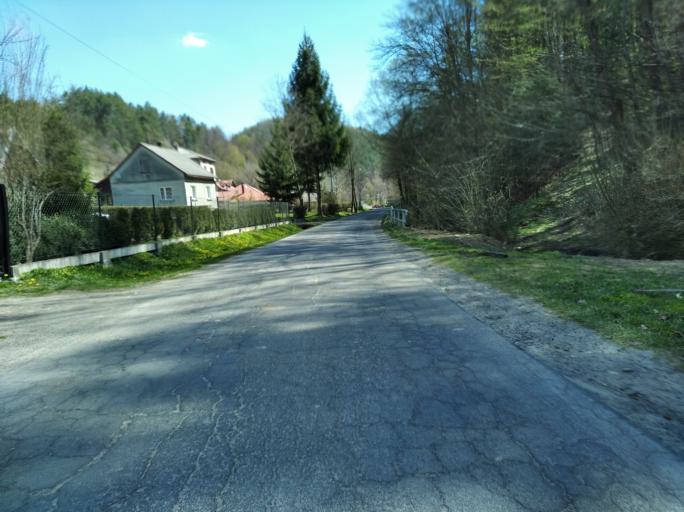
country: PL
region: Subcarpathian Voivodeship
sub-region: Powiat brzozowski
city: Dydnia
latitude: 49.7152
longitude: 22.1825
